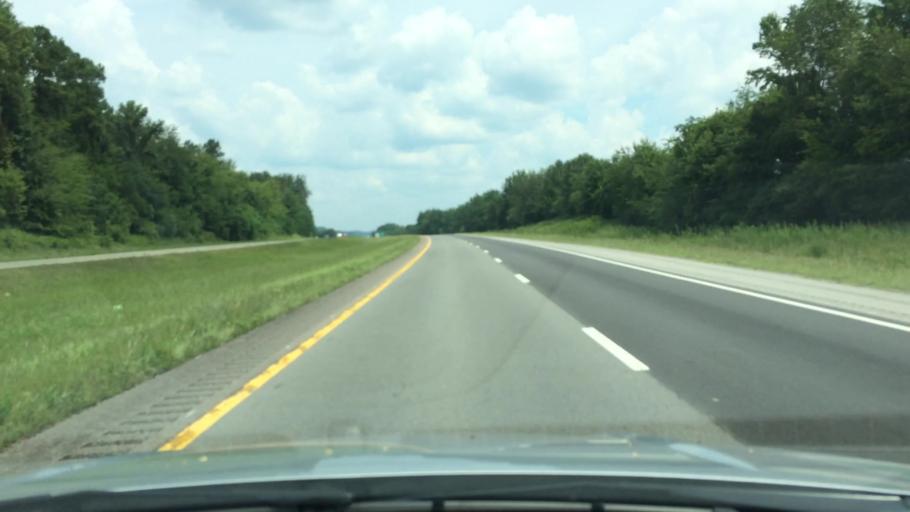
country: US
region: Tennessee
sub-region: Marshall County
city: Cornersville
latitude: 35.2976
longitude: -86.8828
